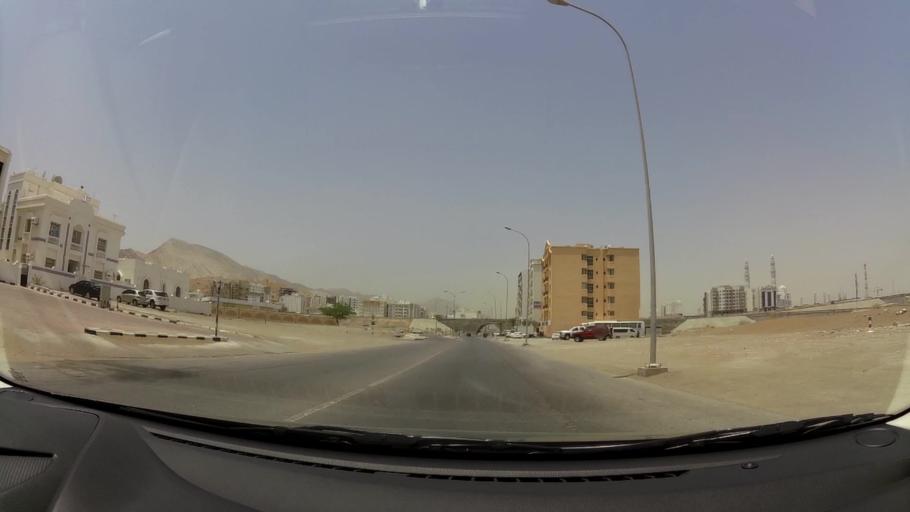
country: OM
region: Muhafazat Masqat
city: Bawshar
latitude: 23.5810
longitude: 58.4212
